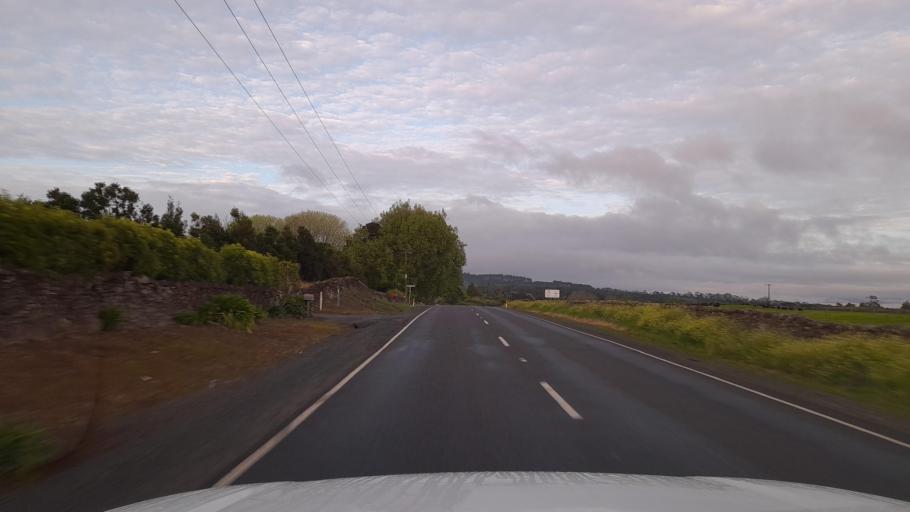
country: NZ
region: Northland
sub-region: Whangarei
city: Maungatapere
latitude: -35.7549
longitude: 174.1856
